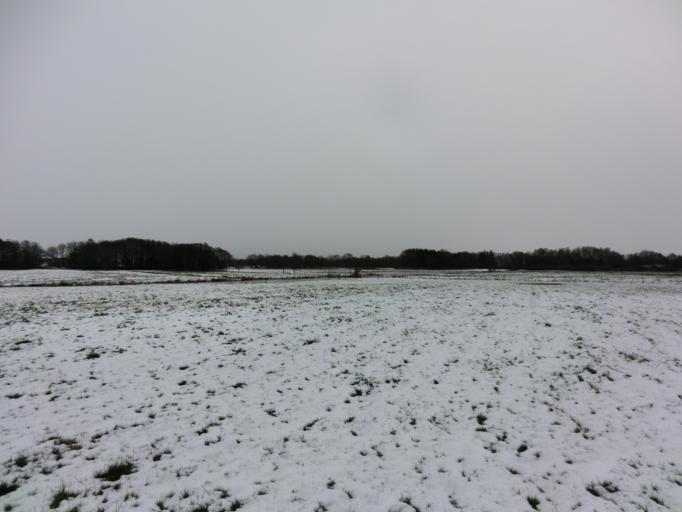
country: SE
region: Skane
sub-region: Hoors Kommun
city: Loberod
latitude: 55.7287
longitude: 13.4030
